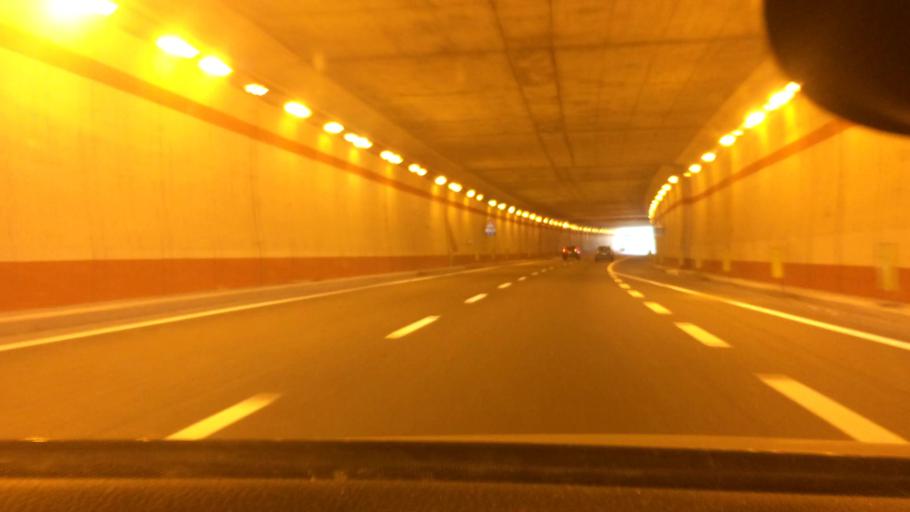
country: IT
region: Lombardy
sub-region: Citta metropolitana di Milano
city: Castano Primo
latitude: 45.5644
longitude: 8.7801
